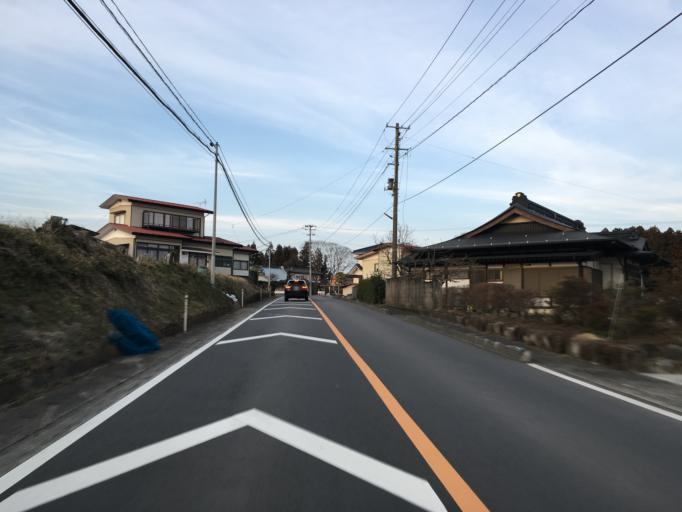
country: JP
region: Ibaraki
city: Daigo
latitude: 36.9491
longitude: 140.4082
